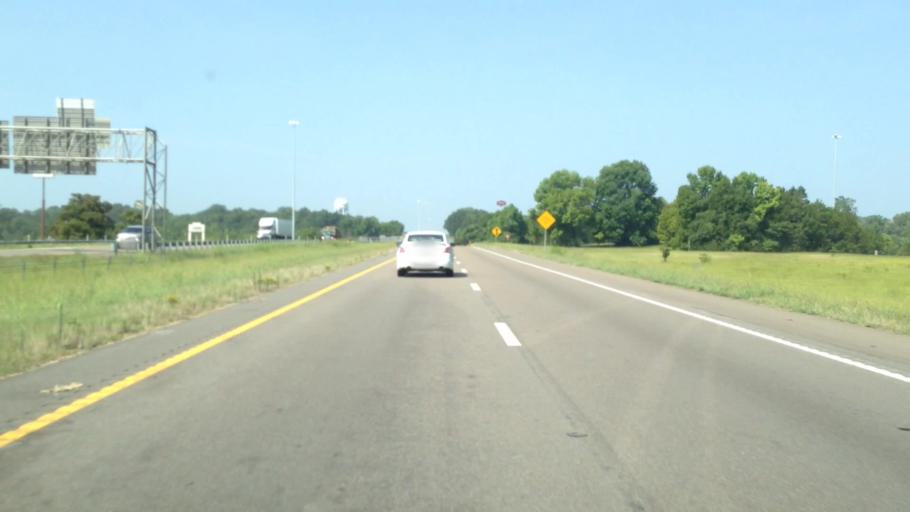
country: US
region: Mississippi
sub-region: Warren County
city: Beechwood
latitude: 32.3452
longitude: -90.8405
